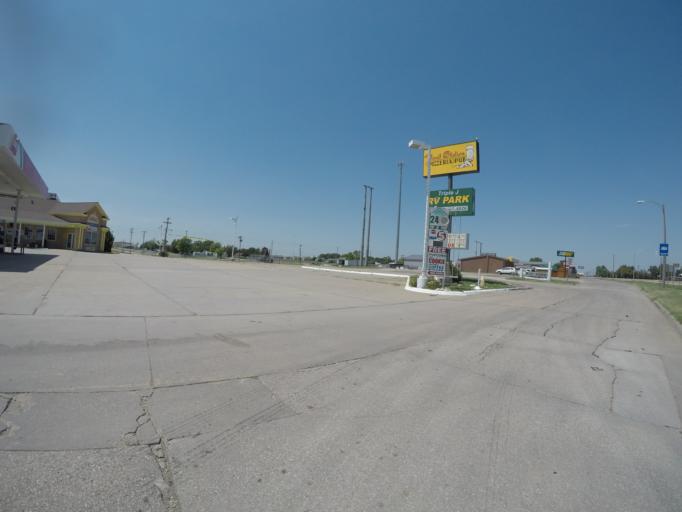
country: US
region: Kansas
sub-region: Russell County
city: Russell
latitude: 38.8660
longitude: -98.8549
